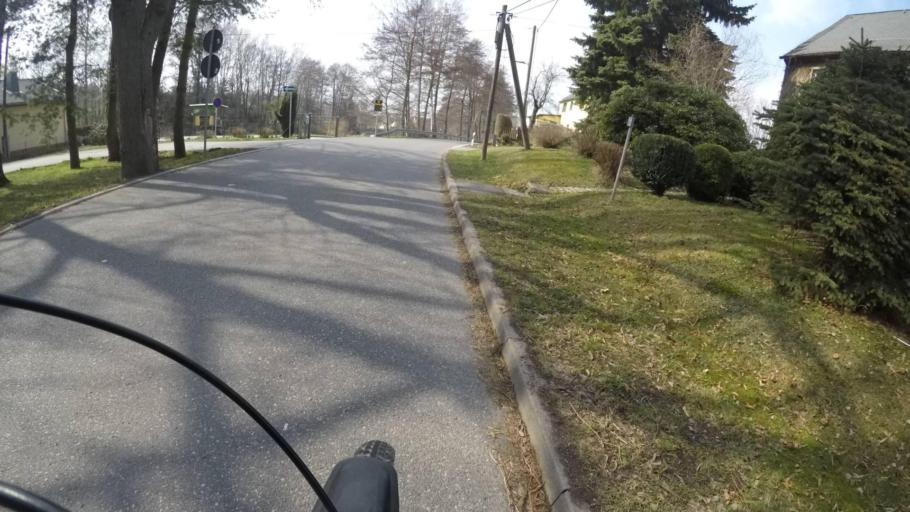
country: DE
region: Saxony
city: Limbach-Oberfrohna
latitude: 50.8298
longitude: 12.7505
